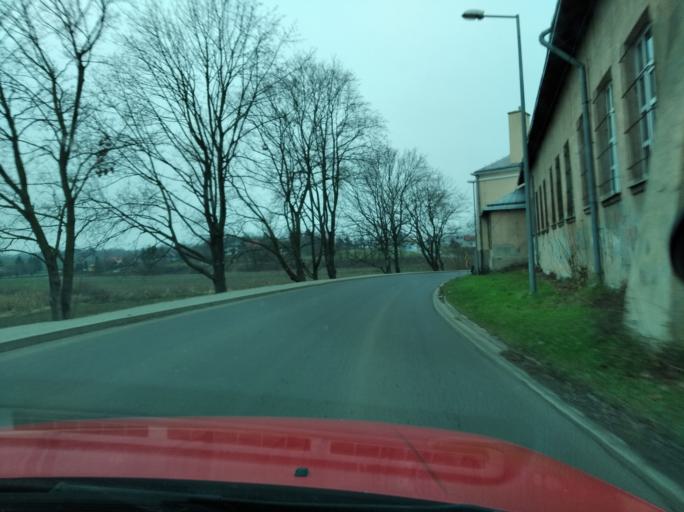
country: PL
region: Subcarpathian Voivodeship
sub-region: Powiat jaroslawski
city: Pawlosiow
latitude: 50.0085
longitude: 22.6543
